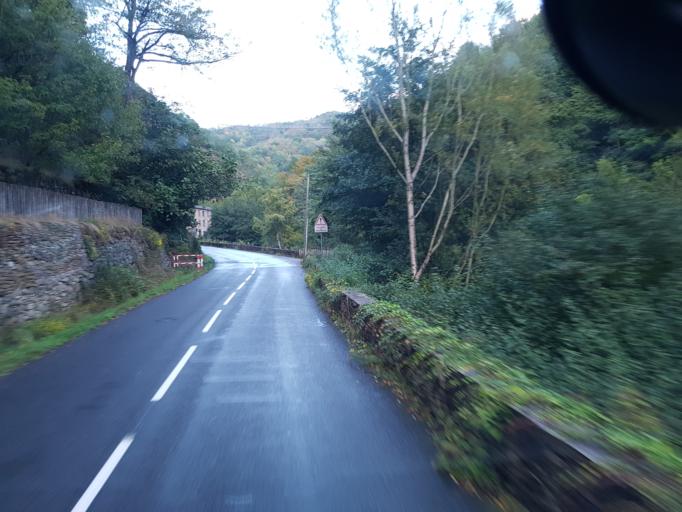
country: FR
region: Midi-Pyrenees
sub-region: Departement du Tarn
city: Mazamet
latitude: 43.4760
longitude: 2.3742
